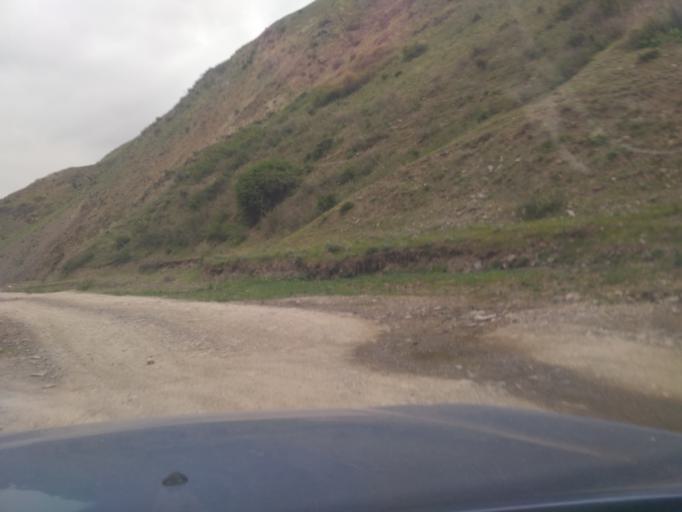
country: UZ
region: Jizzax
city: Zomin
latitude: 39.8533
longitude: 68.3928
